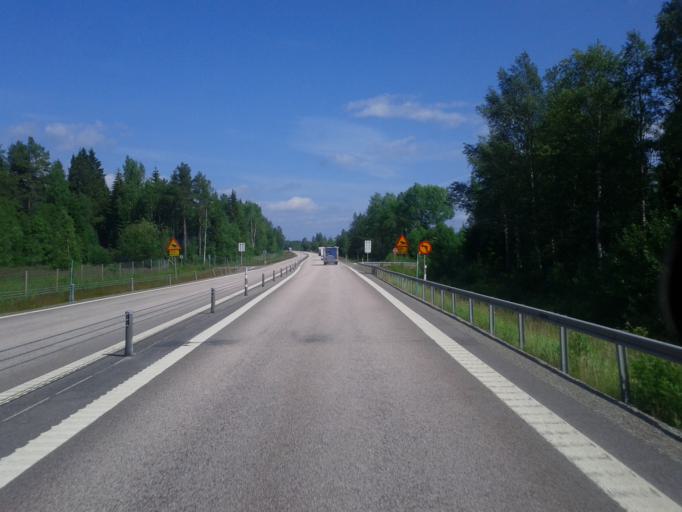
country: SE
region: Vaesterbotten
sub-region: Nordmalings Kommun
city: Nordmaling
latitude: 63.5215
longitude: 19.3791
